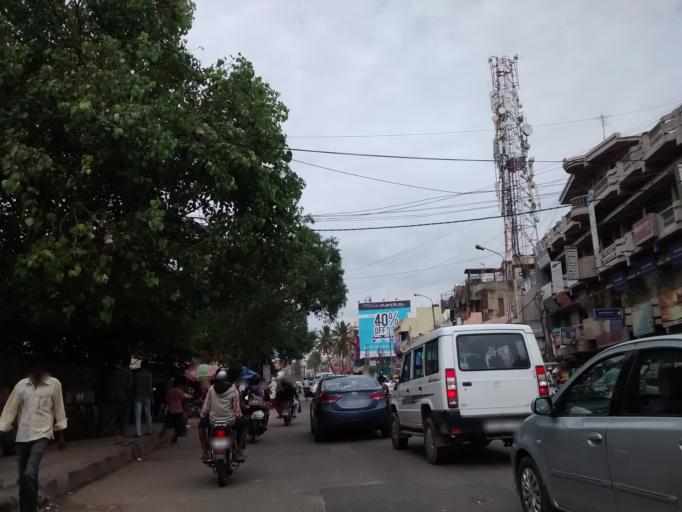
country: IN
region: Karnataka
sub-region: Bangalore Urban
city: Bangalore
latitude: 12.9562
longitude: 77.6938
